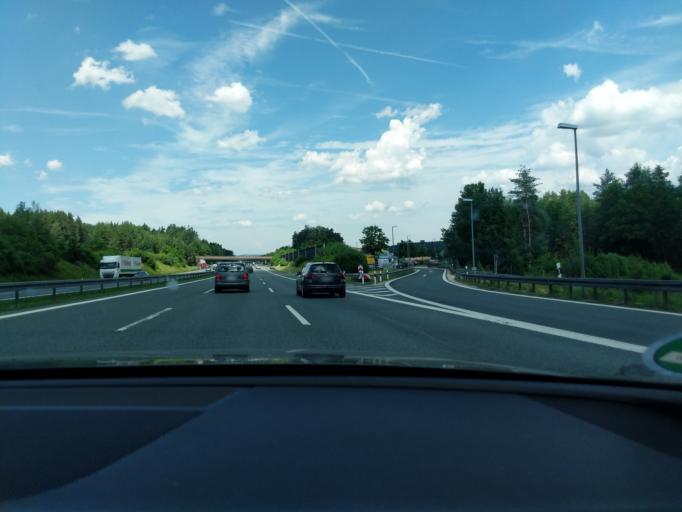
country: DE
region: Bavaria
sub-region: Upper Franconia
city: Haag
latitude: 49.8924
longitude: 11.5996
